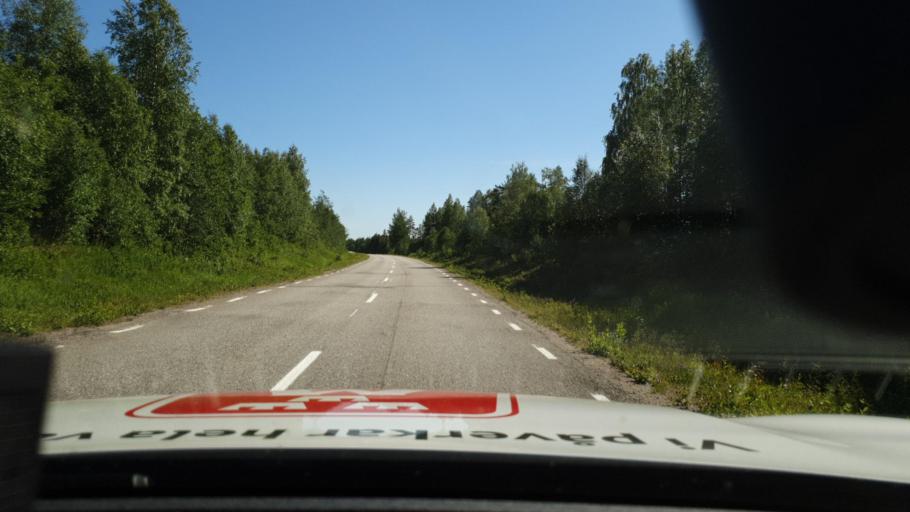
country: SE
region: Norrbotten
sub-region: Lulea Kommun
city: Ranea
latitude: 66.0225
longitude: 22.2983
